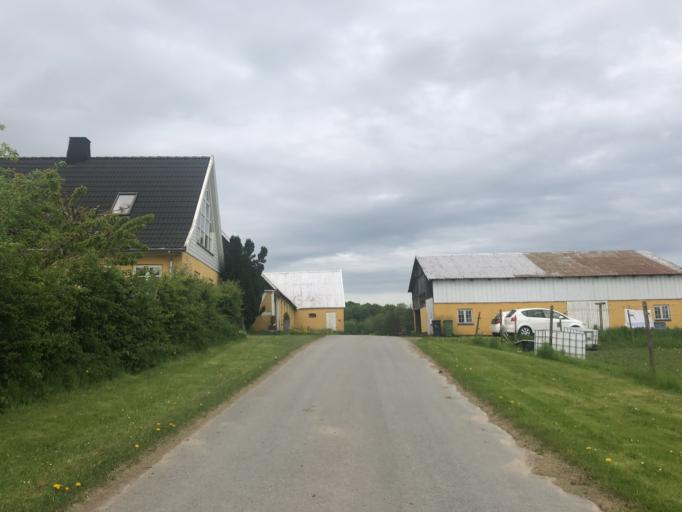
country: DK
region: Zealand
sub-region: Koge Kommune
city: Bjaeverskov
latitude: 55.4290
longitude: 12.0799
